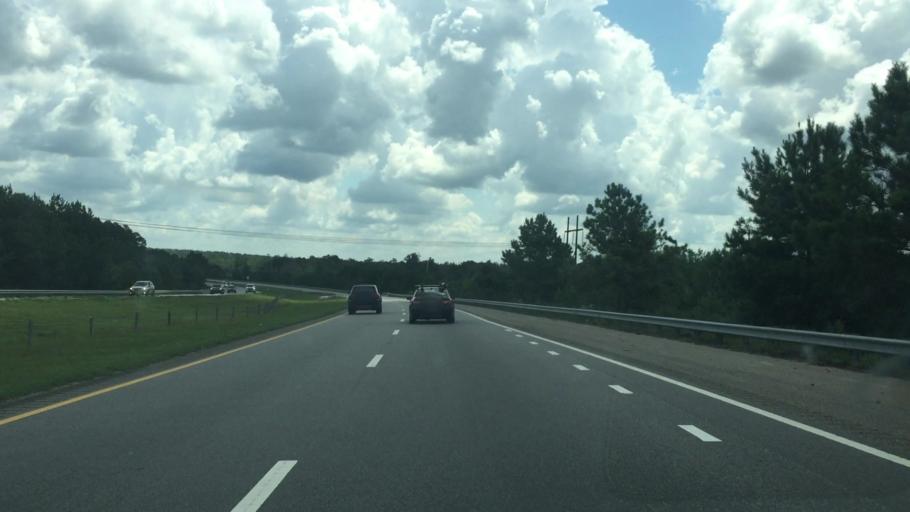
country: US
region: North Carolina
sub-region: Richmond County
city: Hamlet
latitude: 34.8532
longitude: -79.7358
